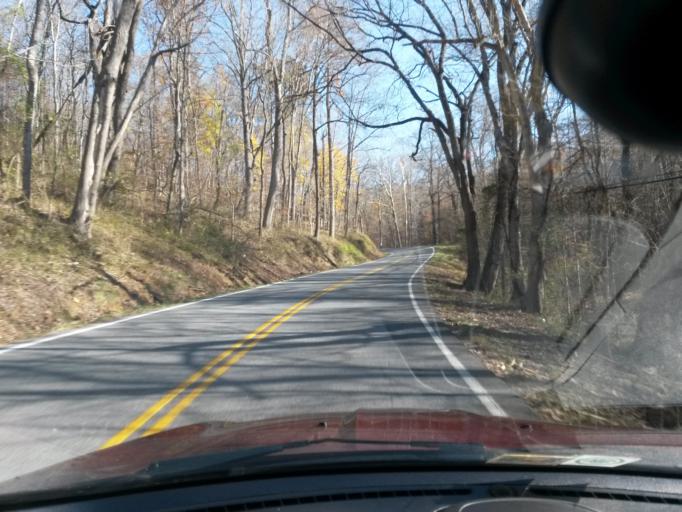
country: US
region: Virginia
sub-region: Botetourt County
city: Buchanan
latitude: 37.6407
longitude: -79.7940
